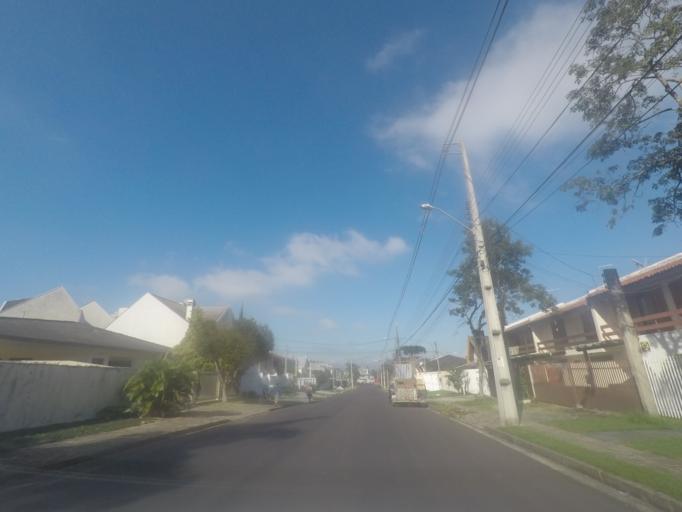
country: BR
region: Parana
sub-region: Pinhais
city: Pinhais
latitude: -25.4593
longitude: -49.2261
